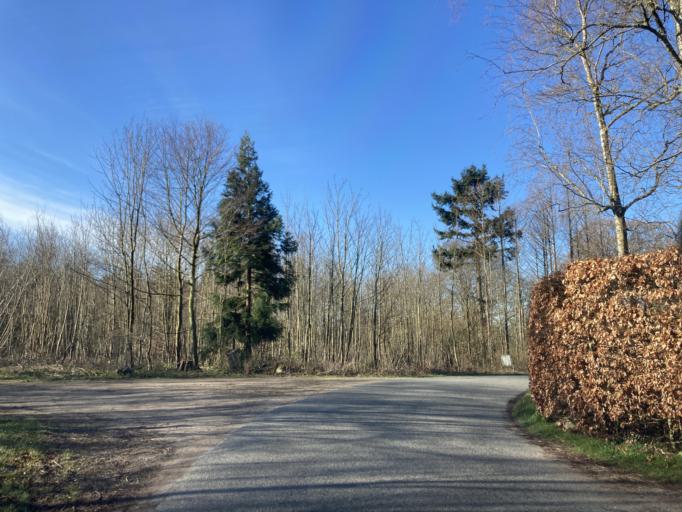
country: DK
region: Zealand
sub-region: Ringsted Kommune
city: Ringsted
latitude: 55.4994
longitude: 11.8389
